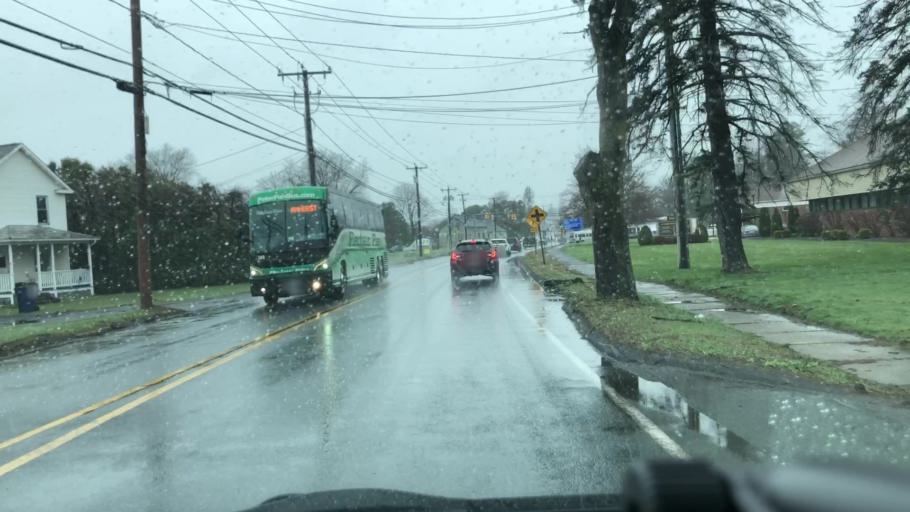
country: US
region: Massachusetts
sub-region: Hampshire County
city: Hadley
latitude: 42.3435
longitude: -72.5802
